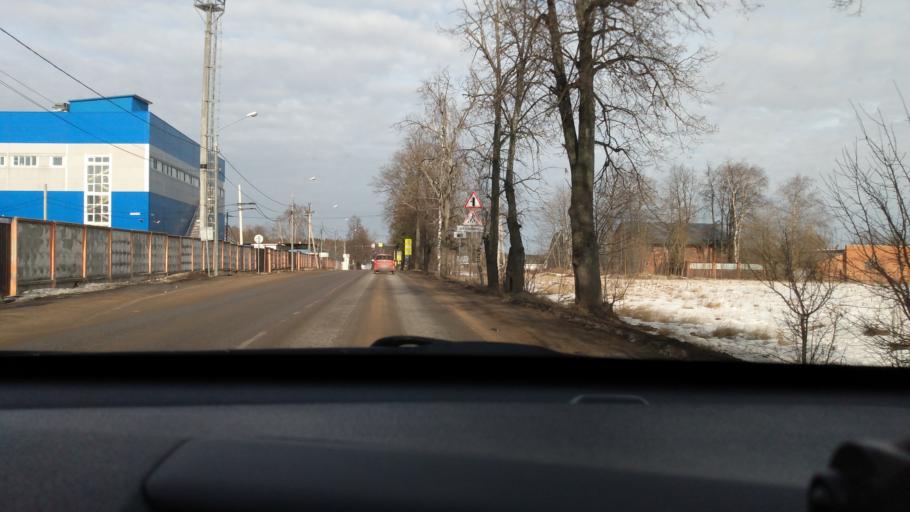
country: RU
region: Moskovskaya
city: Nakhabino
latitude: 55.8625
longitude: 37.1859
